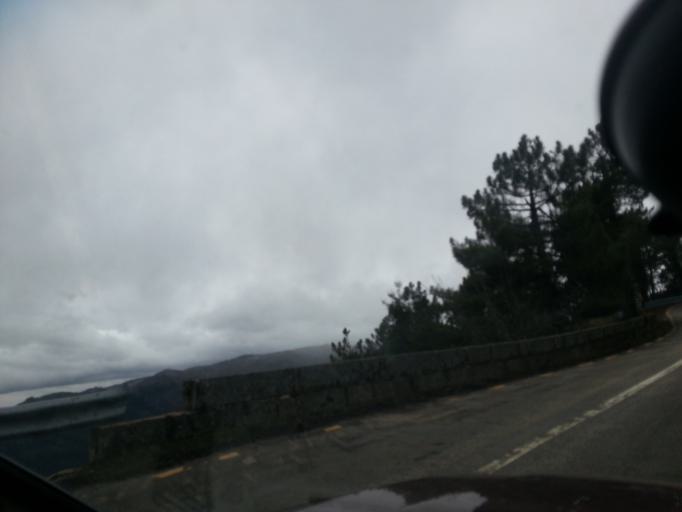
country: PT
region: Guarda
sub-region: Manteigas
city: Manteigas
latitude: 40.4178
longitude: -7.5417
